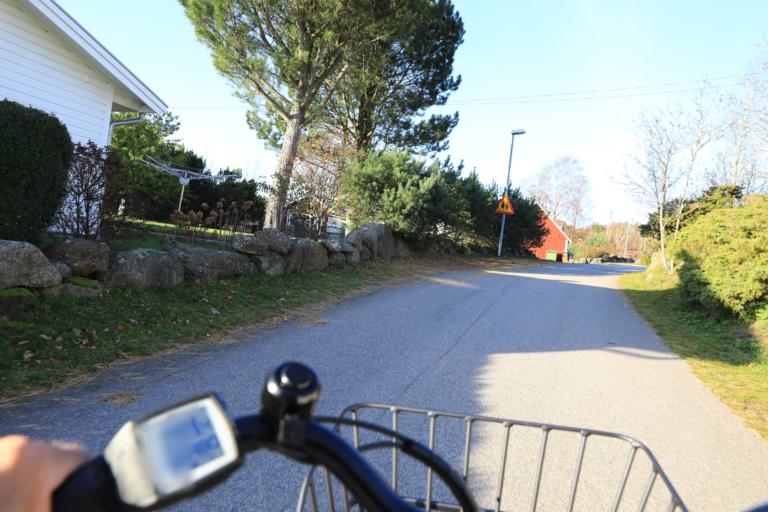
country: SE
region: Halland
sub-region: Varbergs Kommun
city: Varberg
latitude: 57.1723
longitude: 12.2203
